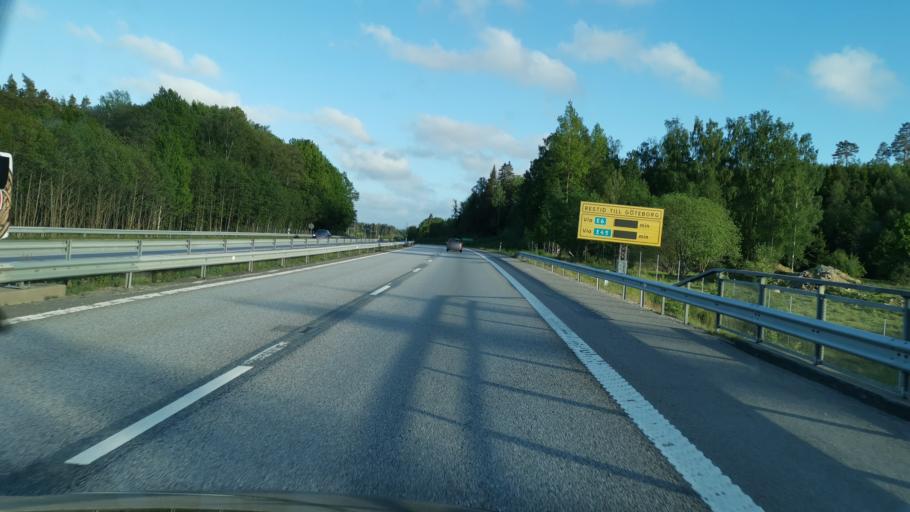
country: SE
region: Vaestra Goetaland
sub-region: Uddevalla Kommun
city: Ljungskile
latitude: 58.2984
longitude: 11.8612
